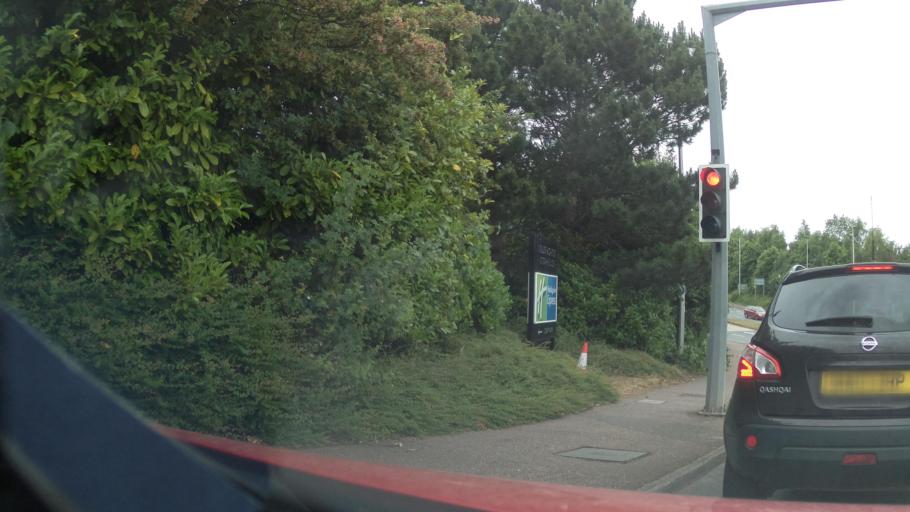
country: GB
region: England
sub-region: Devon
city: Heavitree
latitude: 50.7261
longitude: -3.4703
